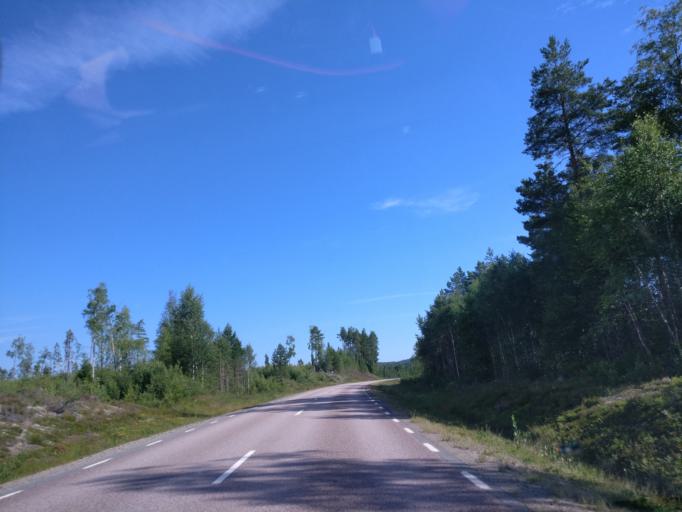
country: SE
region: Vaermland
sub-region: Hagfors Kommun
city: Hagfors
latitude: 60.0369
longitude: 13.9207
